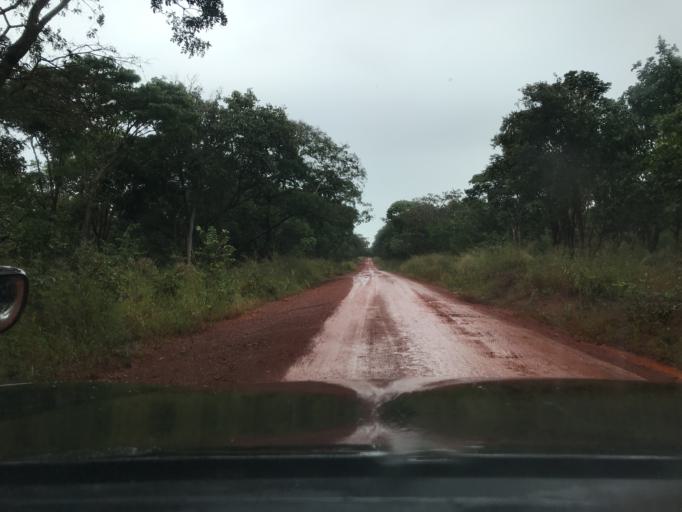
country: TZ
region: Kigoma
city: Uvinza
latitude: -5.2869
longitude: 30.3691
